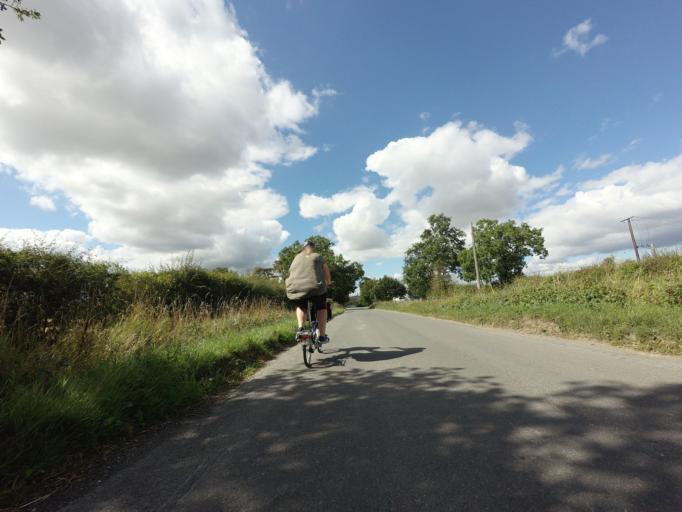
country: GB
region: England
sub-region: Kent
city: Staplehurst
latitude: 51.1528
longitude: 0.5322
